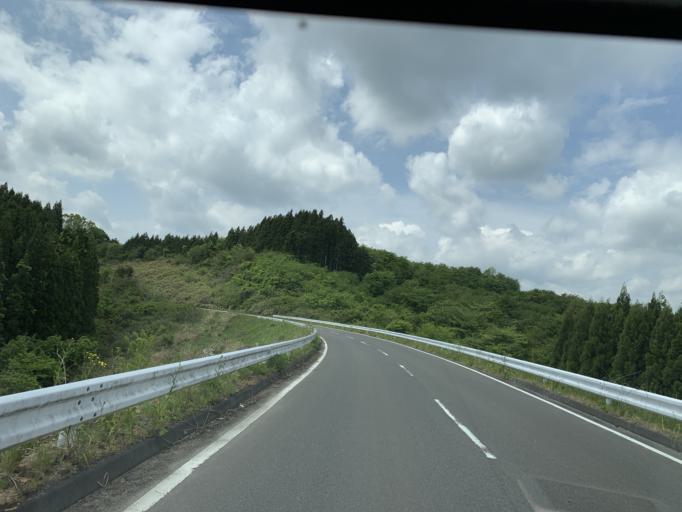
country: JP
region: Miyagi
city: Furukawa
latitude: 38.7197
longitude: 140.9207
